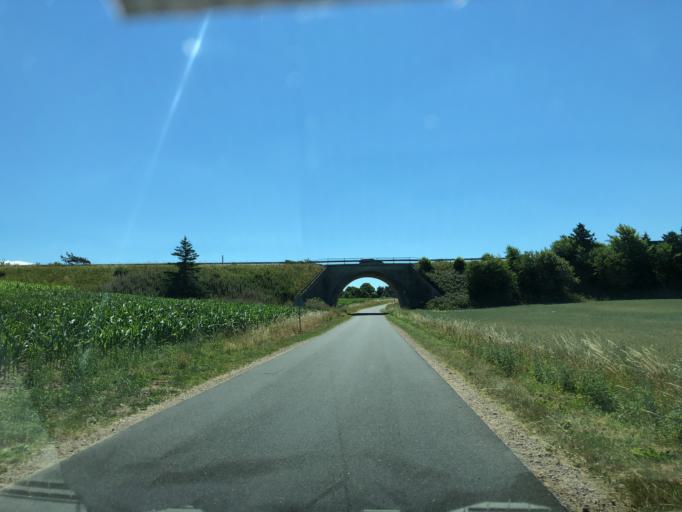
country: DK
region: Central Jutland
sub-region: Viborg Kommune
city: Viborg
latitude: 56.5403
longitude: 9.4678
